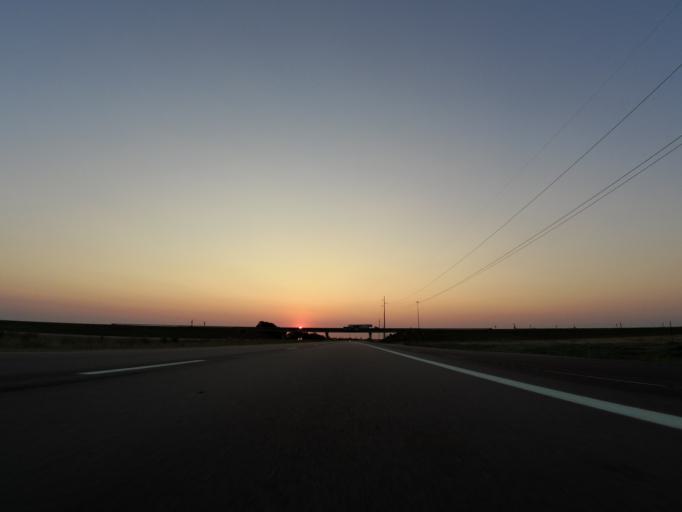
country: US
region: Kansas
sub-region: Reno County
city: South Hutchinson
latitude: 38.0131
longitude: -97.9702
